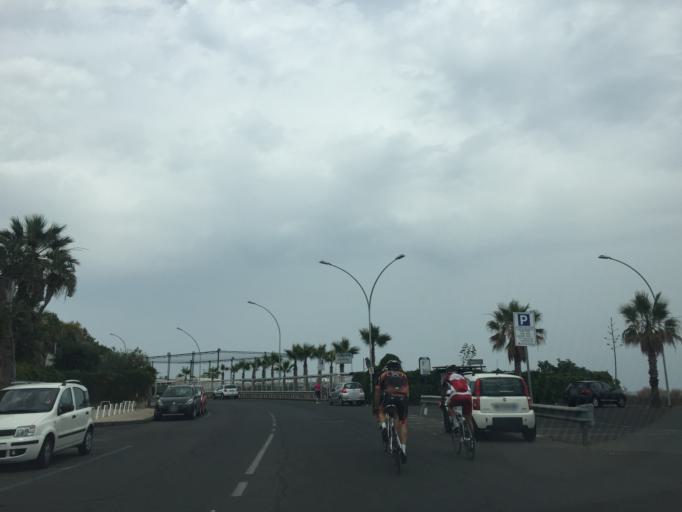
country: IT
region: Sicily
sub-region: Catania
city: Aci Castello
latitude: 37.5445
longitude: 15.1431
